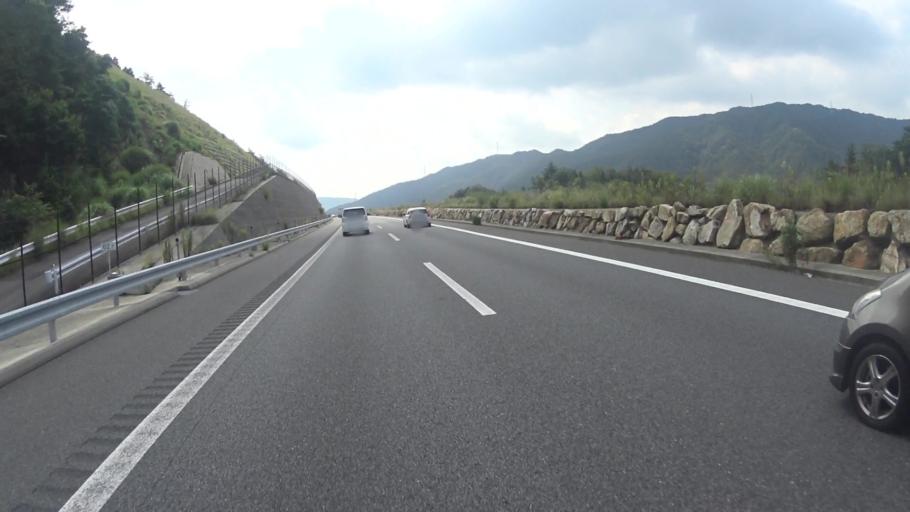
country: JP
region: Shiga Prefecture
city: Kusatsu
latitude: 34.9365
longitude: 136.0391
